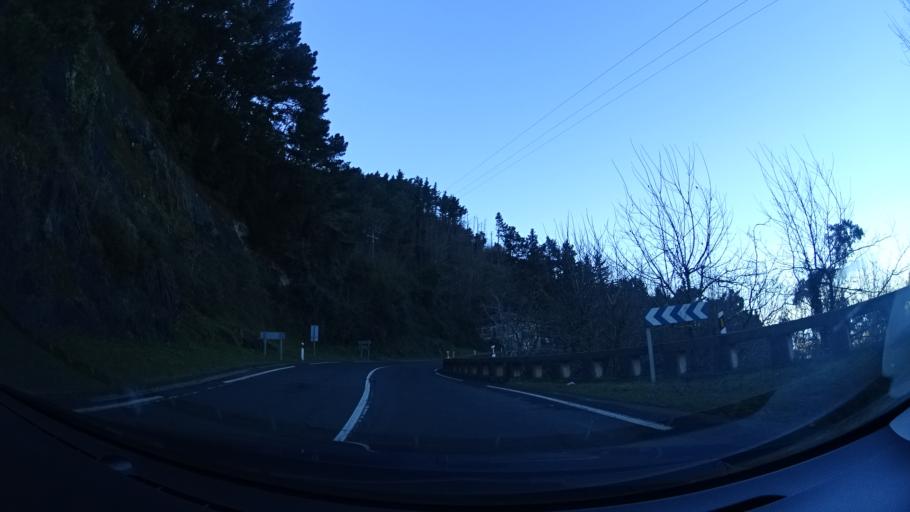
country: ES
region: Basque Country
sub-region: Bizkaia
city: Ondarroa
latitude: 43.3181
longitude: -2.4127
